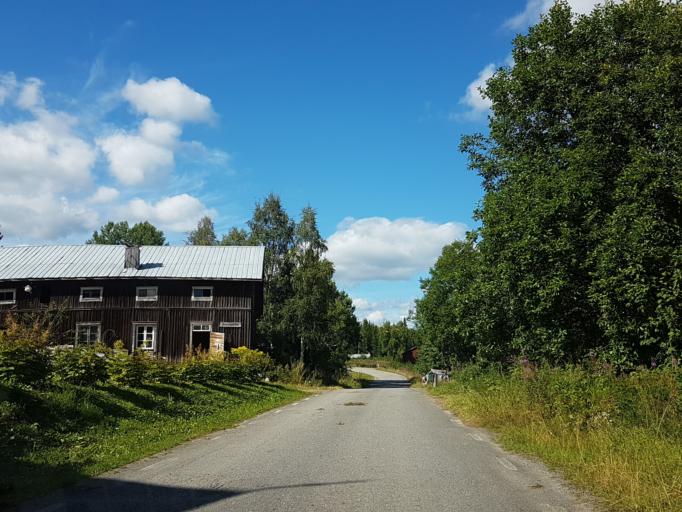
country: SE
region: Vaesterbotten
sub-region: Skelleftea Kommun
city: Burtraesk
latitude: 64.2700
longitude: 20.4911
